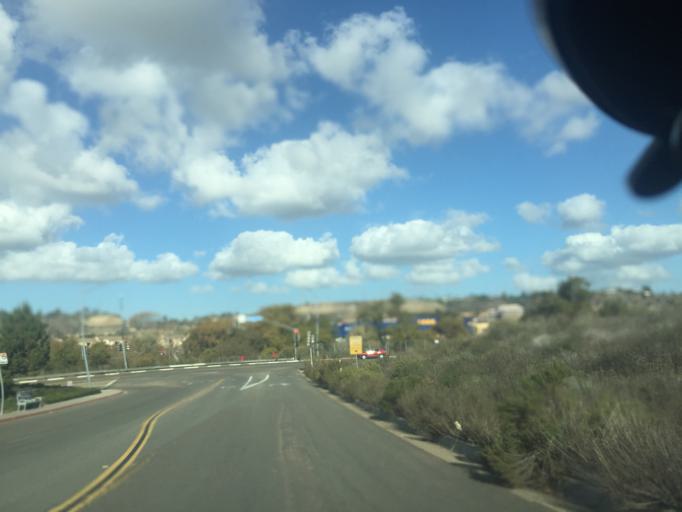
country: US
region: California
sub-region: San Diego County
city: San Diego
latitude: 32.7761
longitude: -117.1253
